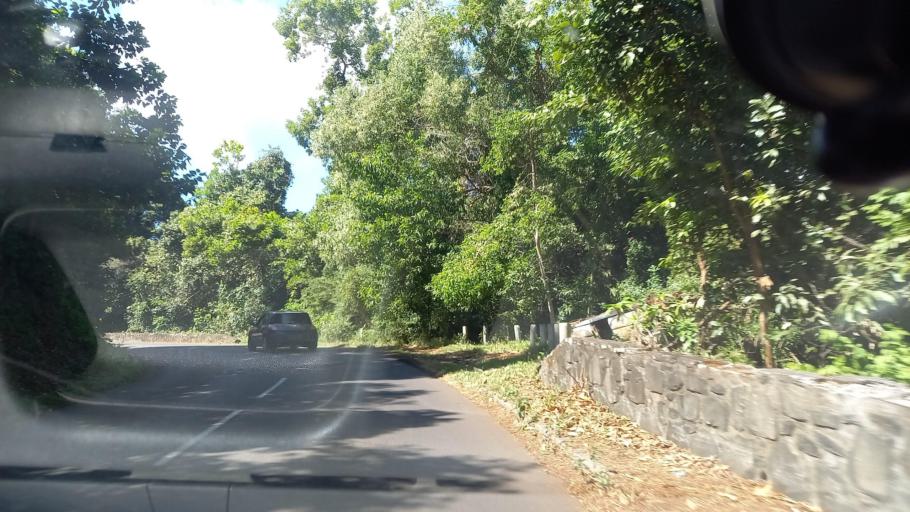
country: YT
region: Tsingoni
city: Tsingoni
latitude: -12.7864
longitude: 45.1523
